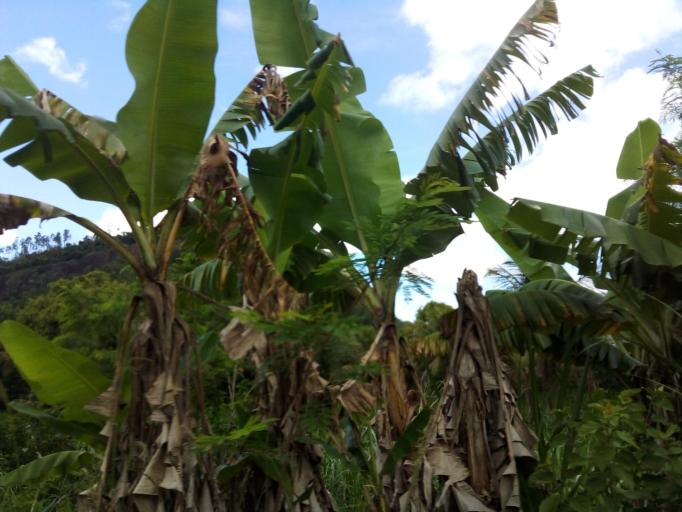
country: BR
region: Espirito Santo
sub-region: Ibiracu
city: Ibiracu
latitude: -19.8698
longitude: -40.3614
